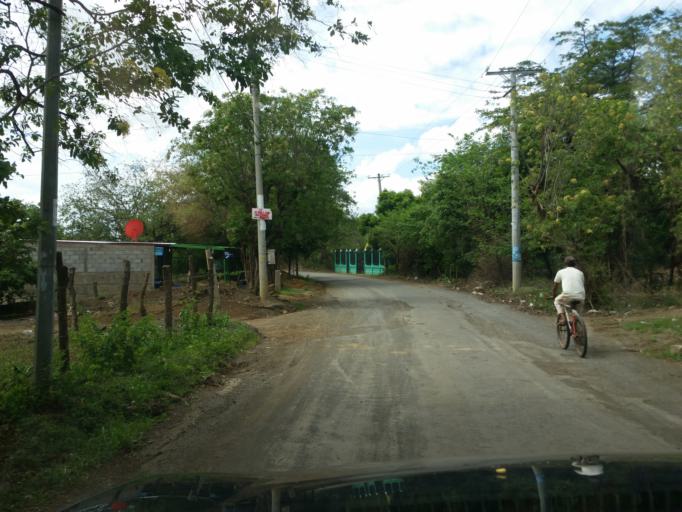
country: NI
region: Masaya
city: Ticuantepe
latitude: 12.0799
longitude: -86.1894
